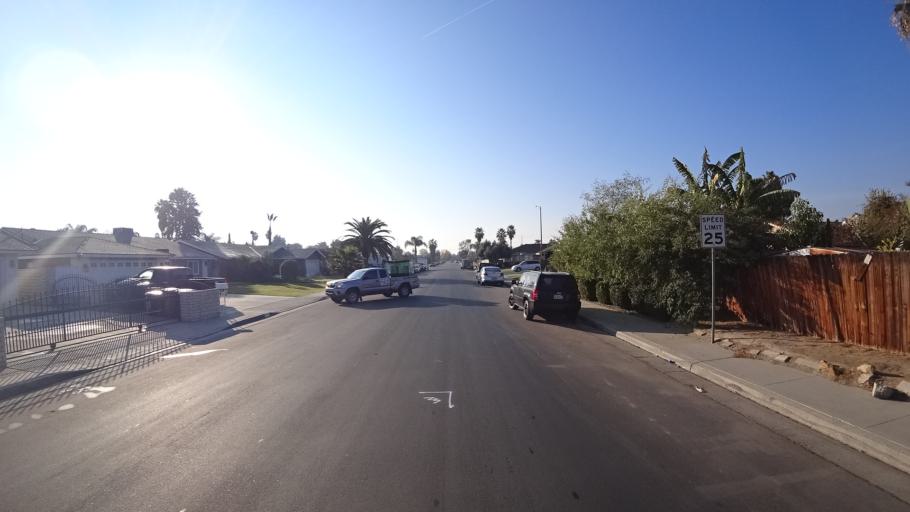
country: US
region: California
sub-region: Kern County
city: Greenfield
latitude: 35.2992
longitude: -119.0236
